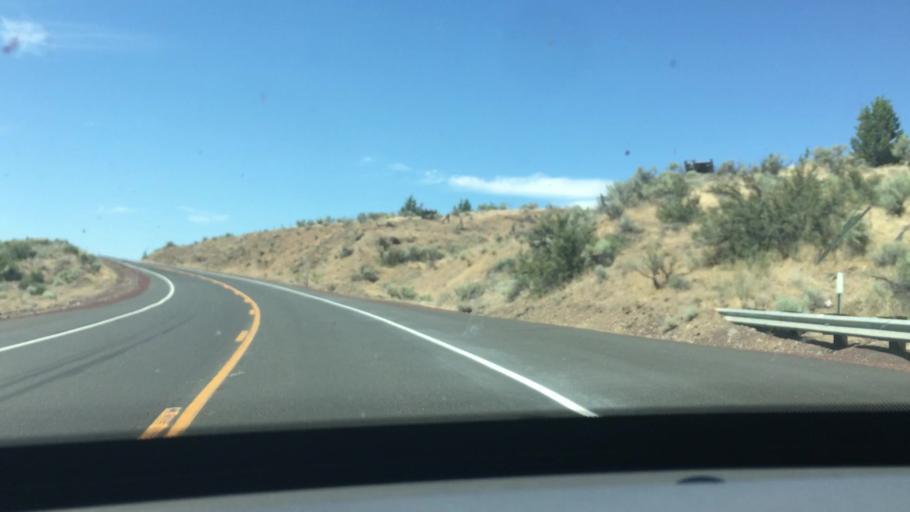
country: US
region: Oregon
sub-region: Sherman County
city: Moro
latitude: 45.0495
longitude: -120.6833
